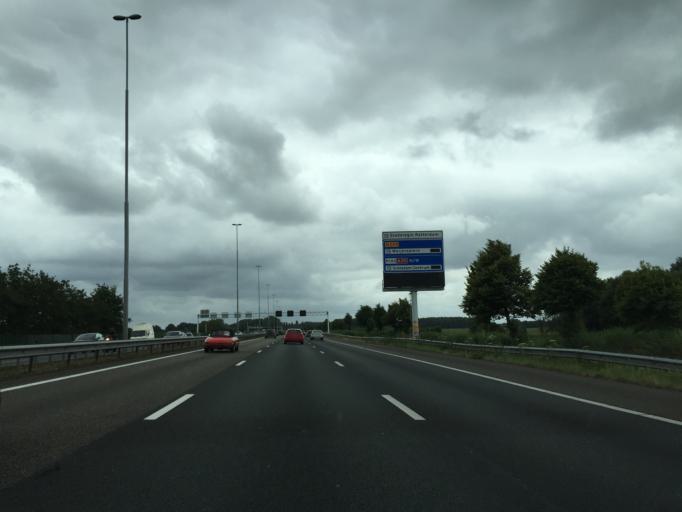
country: NL
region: South Holland
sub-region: Gemeente Delft
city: Delft
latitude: 51.9761
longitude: 4.3976
